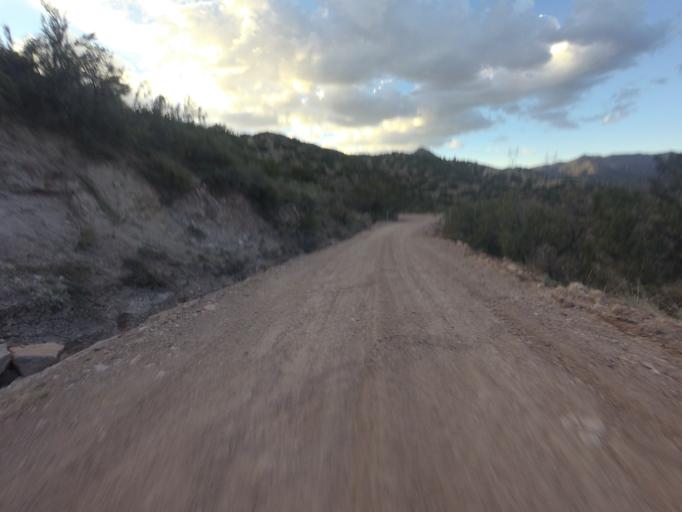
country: US
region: Arizona
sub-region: Gila County
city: Pine
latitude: 34.3746
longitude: -111.6637
